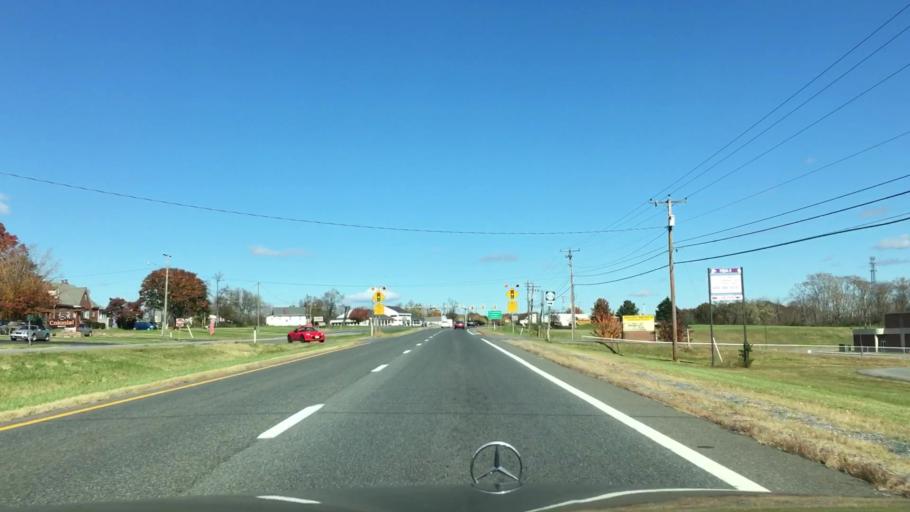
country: US
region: Virginia
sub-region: Campbell County
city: Rustburg
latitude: 37.2510
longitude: -79.1873
